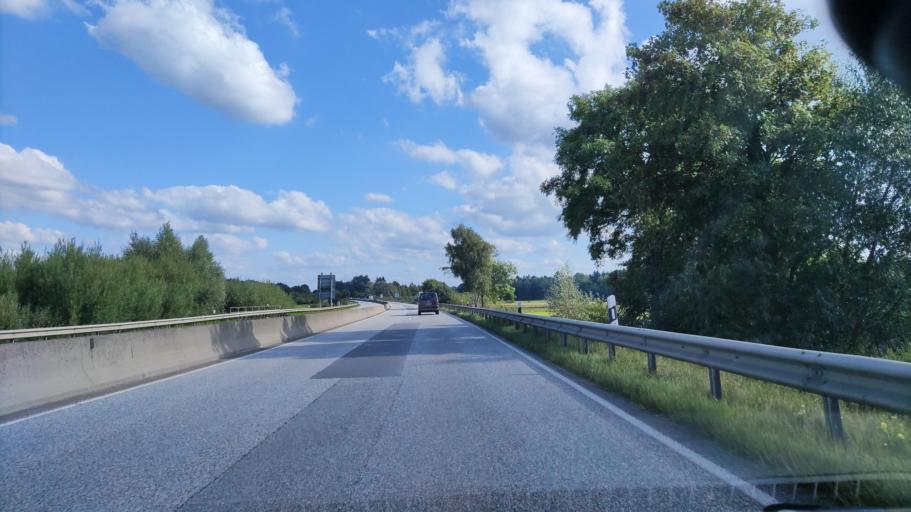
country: DE
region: Schleswig-Holstein
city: Westerronfeld
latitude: 54.3061
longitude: 9.6324
